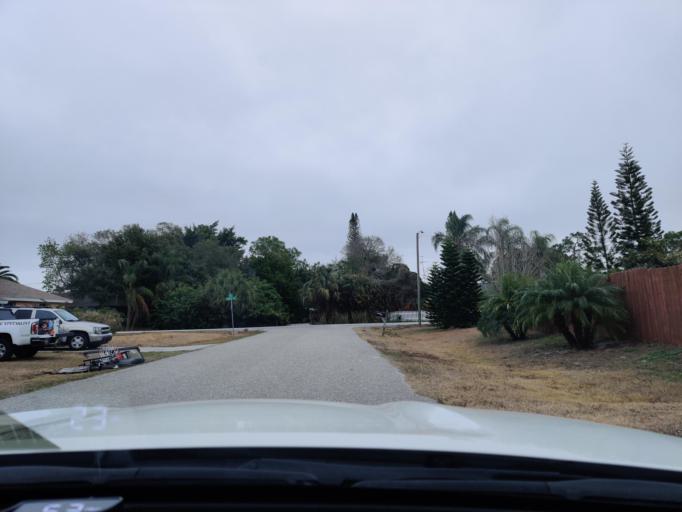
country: US
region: Florida
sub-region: Sarasota County
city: South Venice
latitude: 27.0387
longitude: -82.4028
